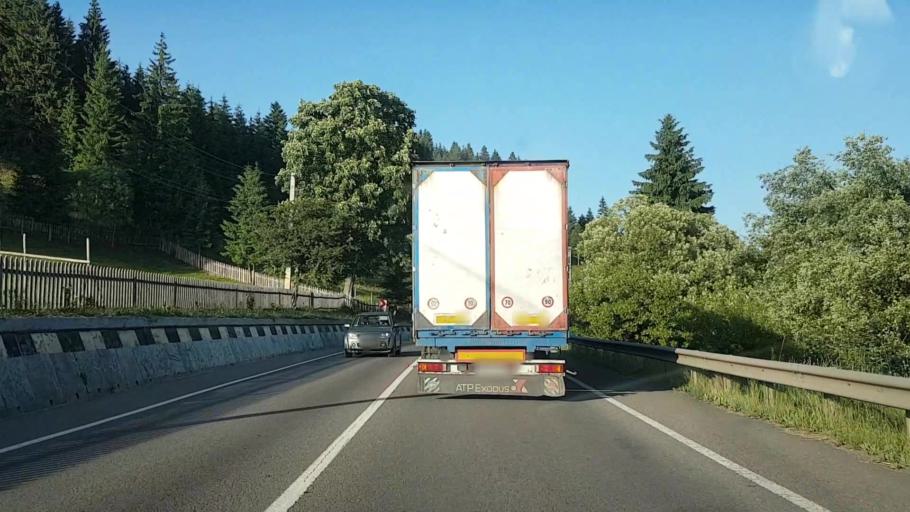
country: RO
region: Suceava
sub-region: Comuna Dorna Candrenilor
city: Dorna Candrenilor
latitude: 47.3572
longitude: 25.2736
